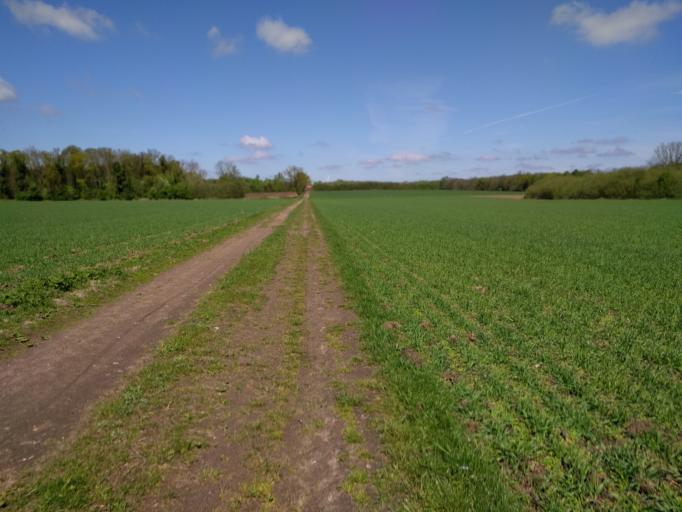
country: DK
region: South Denmark
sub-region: Kerteminde Kommune
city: Langeskov
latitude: 55.3866
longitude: 10.5530
